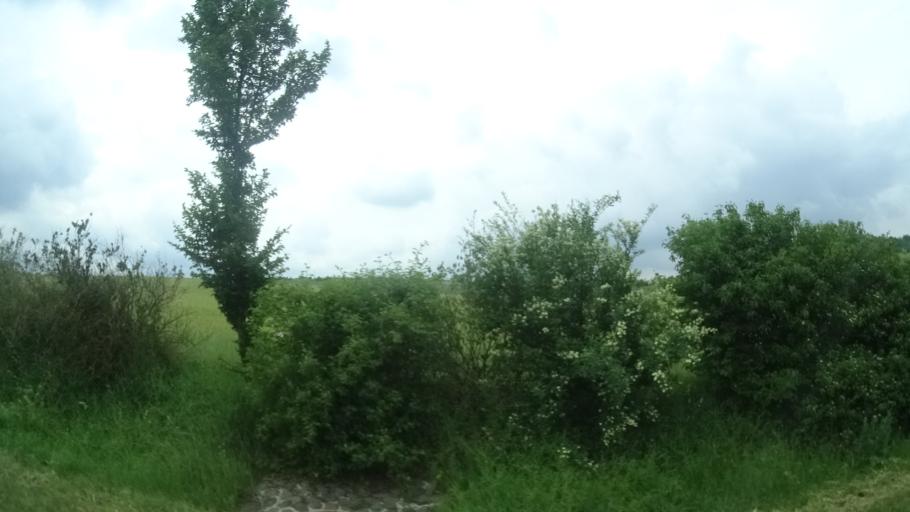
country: DE
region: Hesse
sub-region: Regierungsbezirk Kassel
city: Fulda
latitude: 50.5403
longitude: 9.6199
